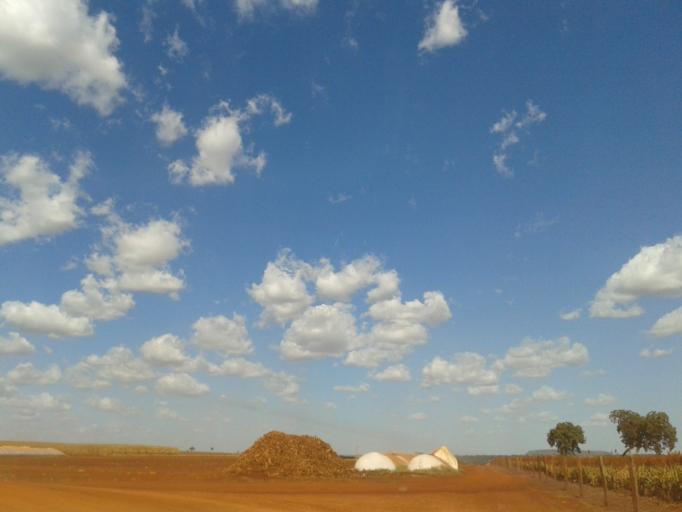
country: BR
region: Minas Gerais
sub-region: Capinopolis
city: Capinopolis
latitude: -18.7014
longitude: -49.6424
